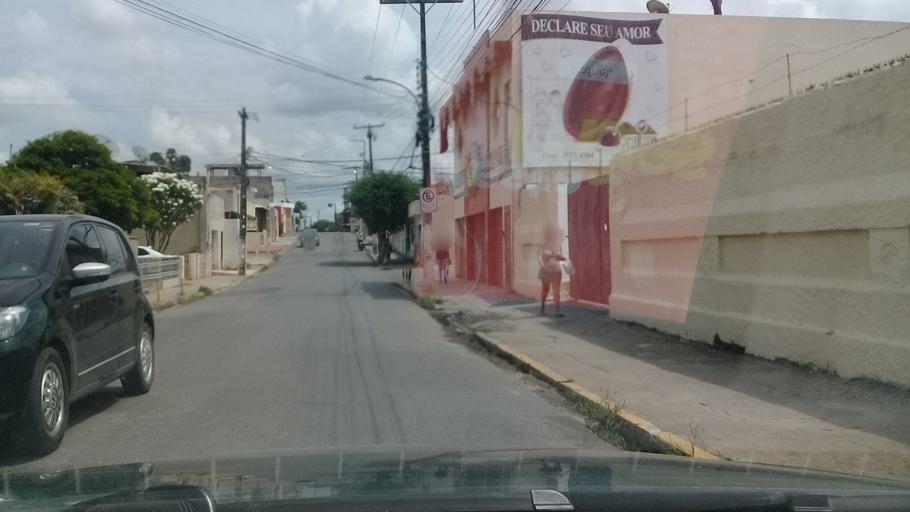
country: BR
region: Pernambuco
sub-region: Vitoria De Santo Antao
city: Vitoria de Santo Antao
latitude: -8.1138
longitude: -35.2898
